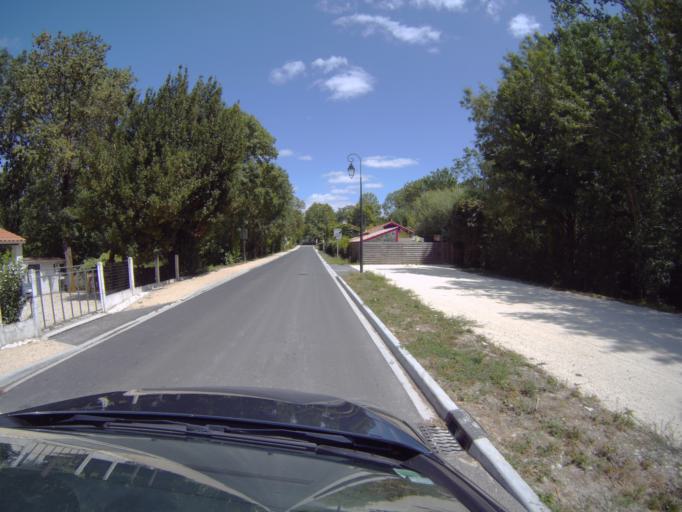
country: FR
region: Poitou-Charentes
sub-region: Departement des Deux-Sevres
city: Saint-Hilaire-la-Palud
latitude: 46.2524
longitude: -0.7574
